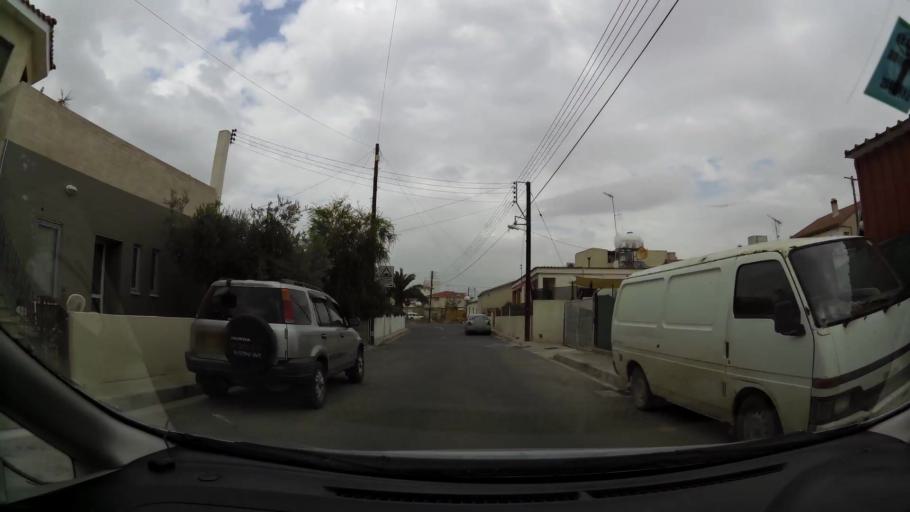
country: CY
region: Lefkosia
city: Geri
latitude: 35.1034
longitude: 33.3730
